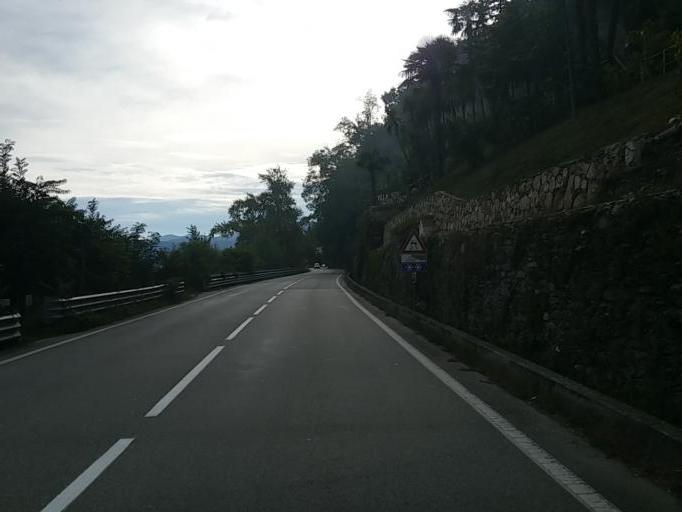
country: IT
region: Piedmont
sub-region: Provincia Verbano-Cusio-Ossola
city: Ghiffa
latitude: 45.9488
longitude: 8.6038
